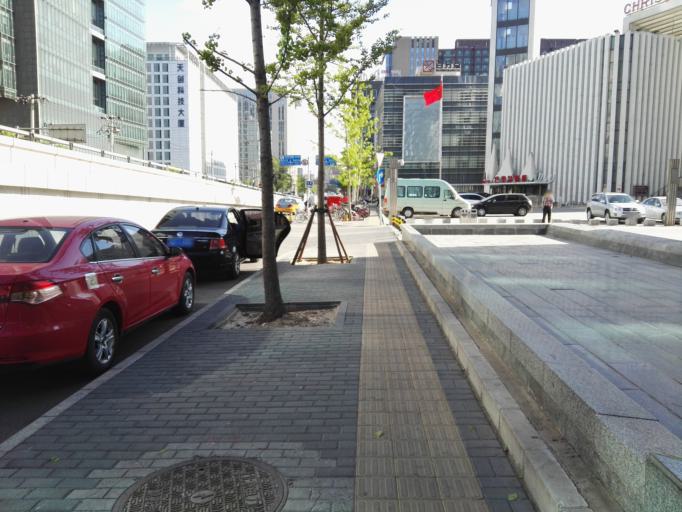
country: CN
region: Beijing
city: Haidian
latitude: 39.9825
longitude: 116.3020
